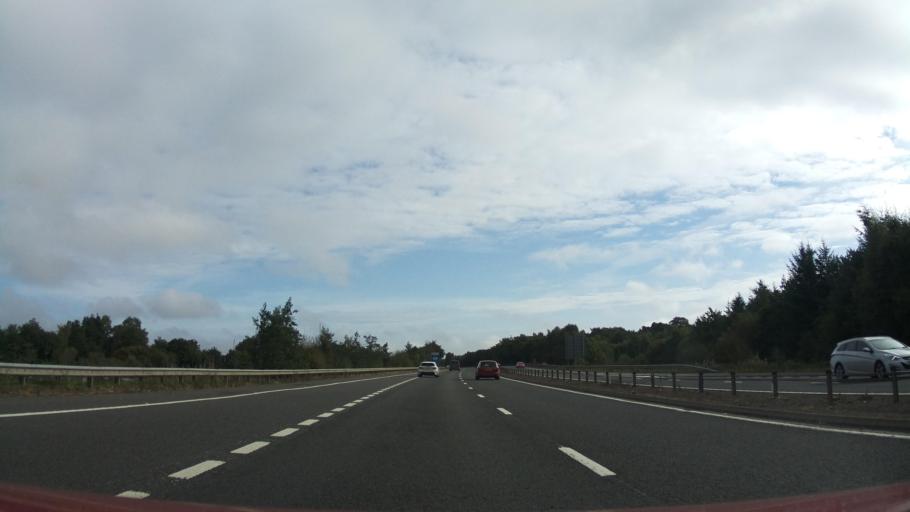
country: GB
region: Scotland
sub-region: Falkirk
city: Larbert
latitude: 56.0345
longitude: -3.8452
